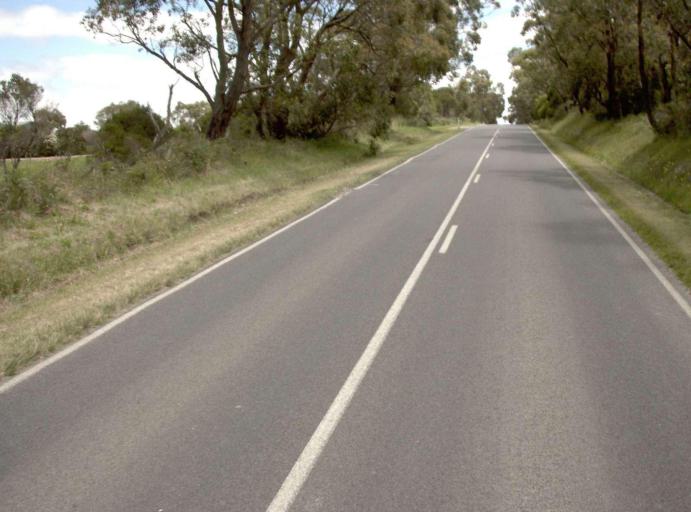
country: AU
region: Victoria
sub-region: Bass Coast
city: North Wonthaggi
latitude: -38.6727
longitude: 146.0291
